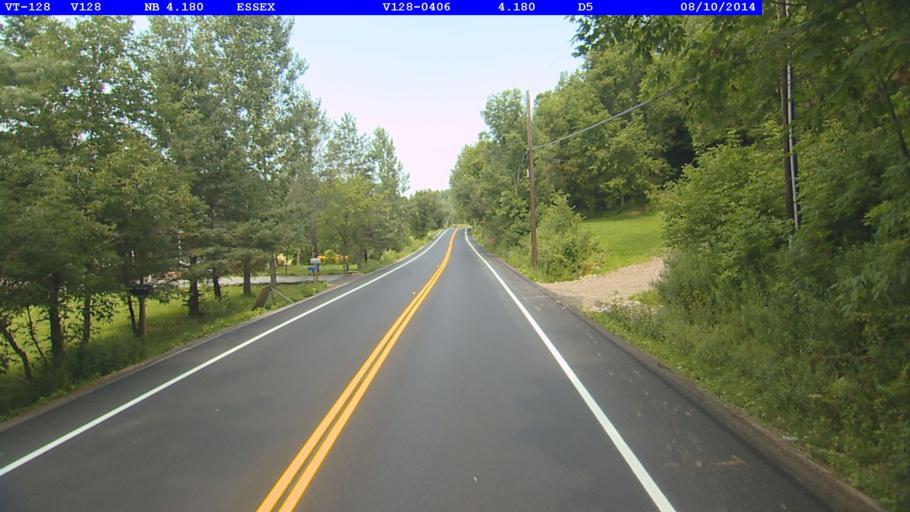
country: US
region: Vermont
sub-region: Chittenden County
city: Jericho
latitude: 44.5567
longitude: -73.0308
